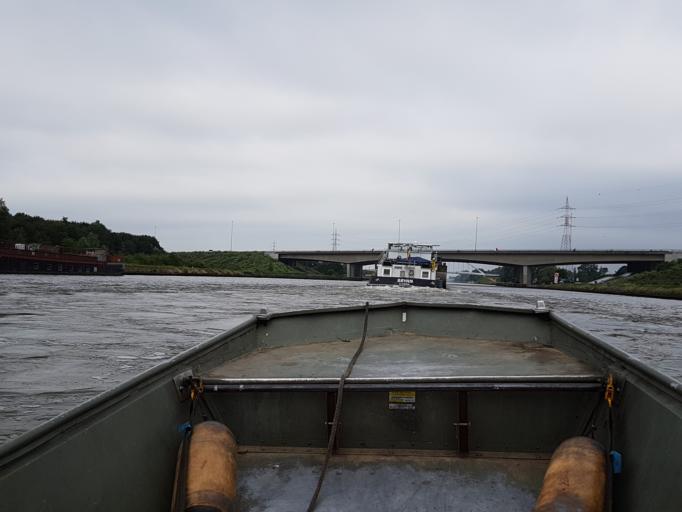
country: BE
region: Flanders
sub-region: Provincie Antwerpen
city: Schilde
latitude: 51.2038
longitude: 4.6096
